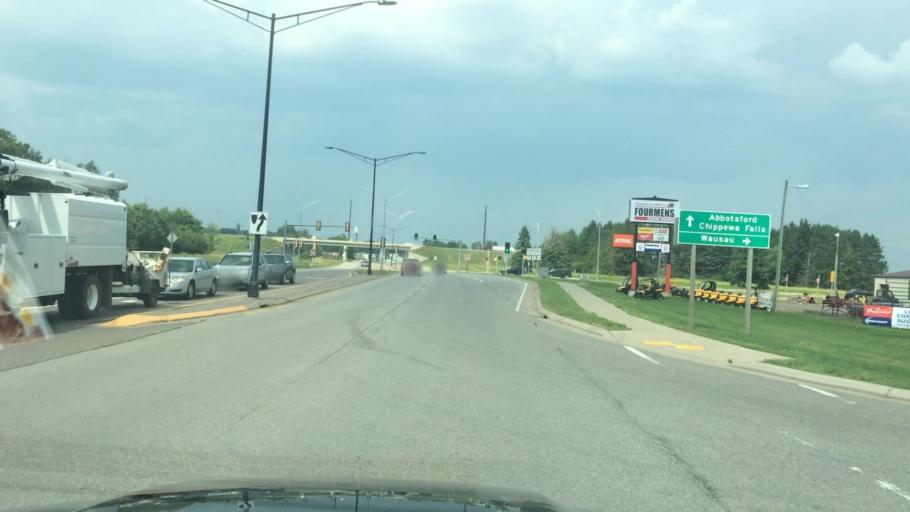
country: US
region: Wisconsin
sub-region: Clark County
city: Abbotsford
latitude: 44.9291
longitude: -90.3154
